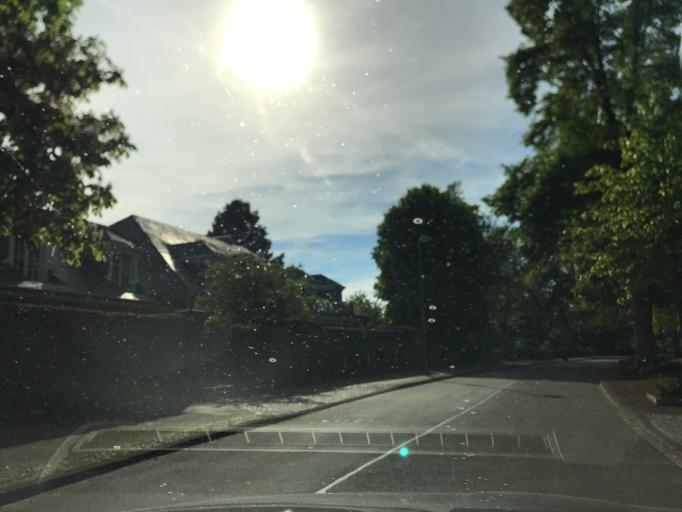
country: DE
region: North Rhine-Westphalia
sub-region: Regierungsbezirk Dusseldorf
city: Essen
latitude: 51.4053
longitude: 6.9781
